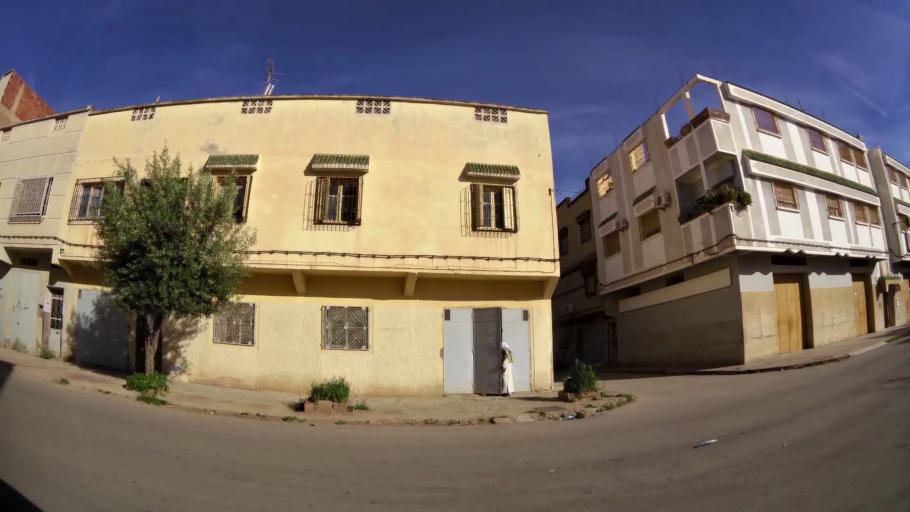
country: MA
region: Oriental
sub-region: Oujda-Angad
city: Oujda
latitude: 34.6730
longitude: -1.8992
